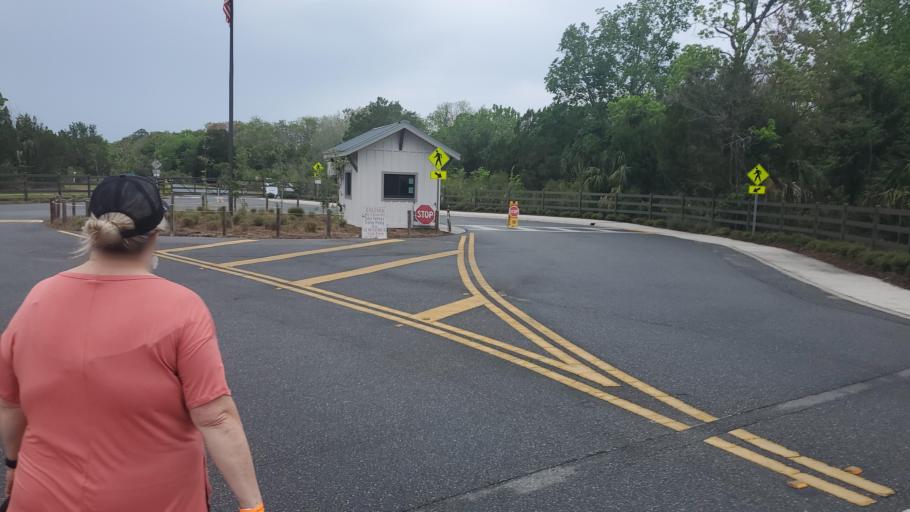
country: US
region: Florida
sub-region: Citrus County
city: Crystal River
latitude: 28.8910
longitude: -82.5873
